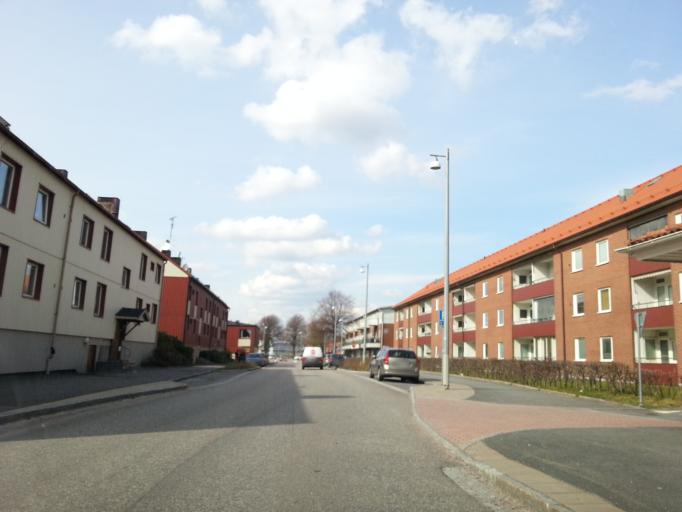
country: SE
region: Vaestra Goetaland
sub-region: Ale Kommun
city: Surte
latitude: 57.8269
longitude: 12.0153
